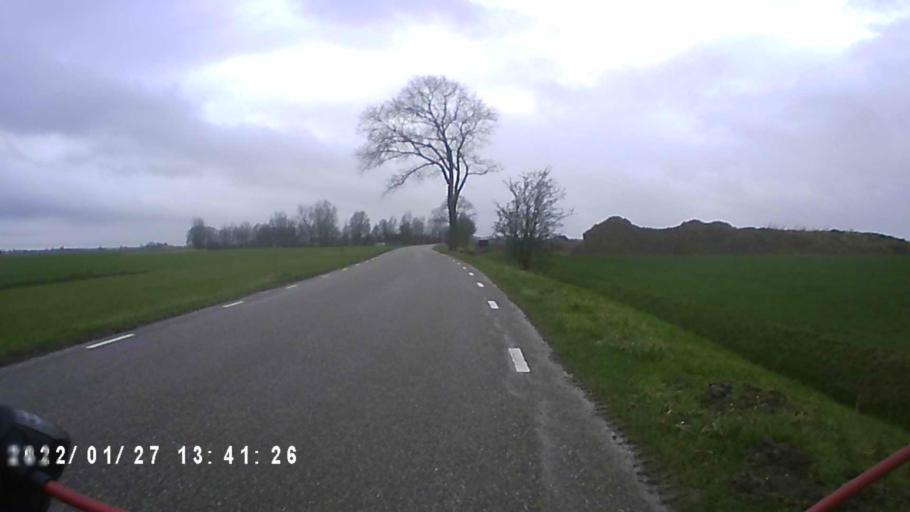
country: NL
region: Friesland
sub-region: Gemeente Kollumerland en Nieuwkruisland
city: Kollum
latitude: 53.3012
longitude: 6.2144
